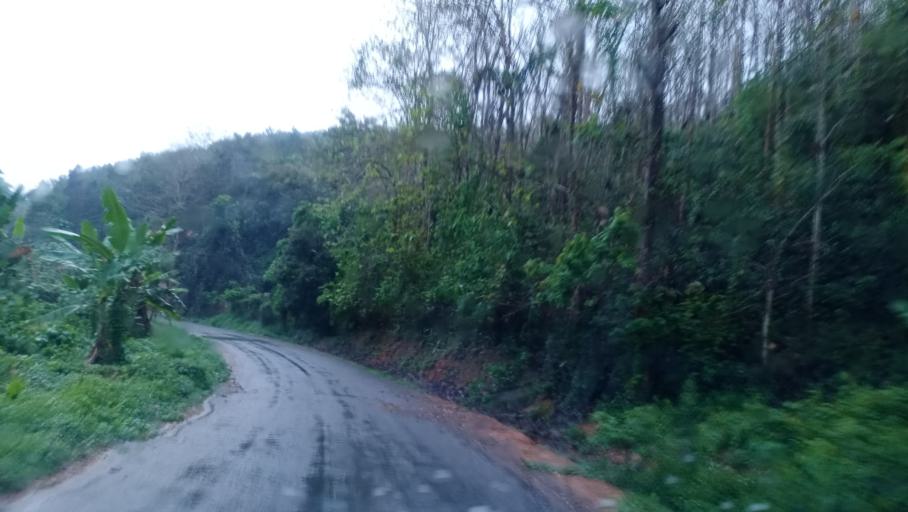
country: LA
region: Phongsali
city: Khoa
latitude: 21.0649
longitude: 102.4768
